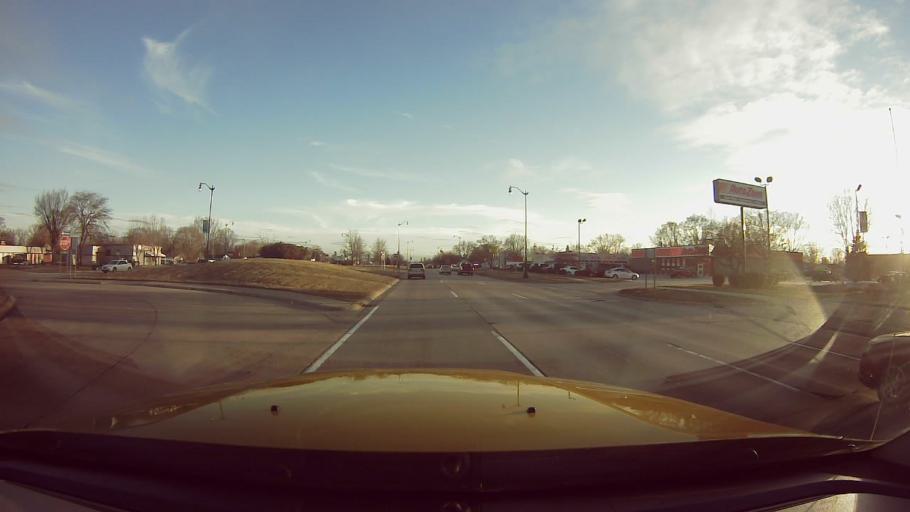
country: US
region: Michigan
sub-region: Wayne County
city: Taylor
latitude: 42.2040
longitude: -83.2686
